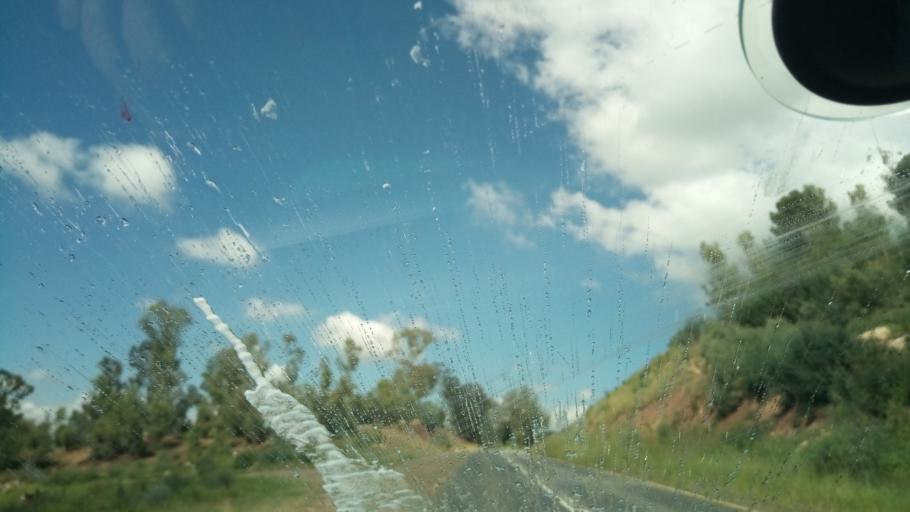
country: ZA
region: Orange Free State
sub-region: Thabo Mofutsanyana District Municipality
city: Ficksburg
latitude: -28.8617
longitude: 27.8748
